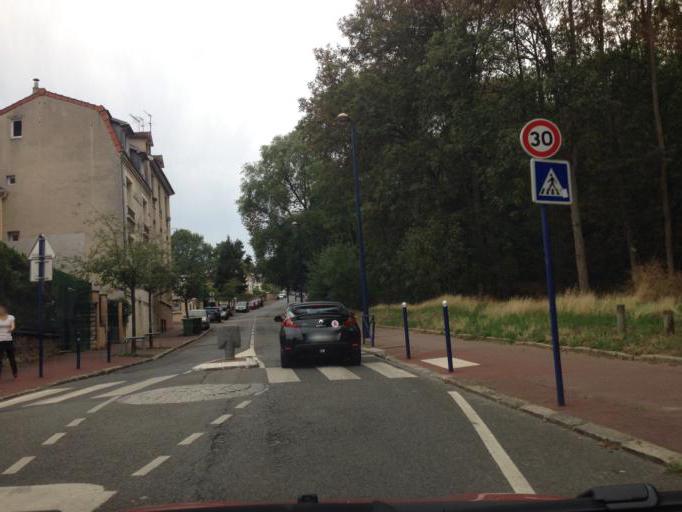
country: FR
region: Ile-de-France
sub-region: Departement des Hauts-de-Seine
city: Clamart
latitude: 48.7959
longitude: 2.2650
